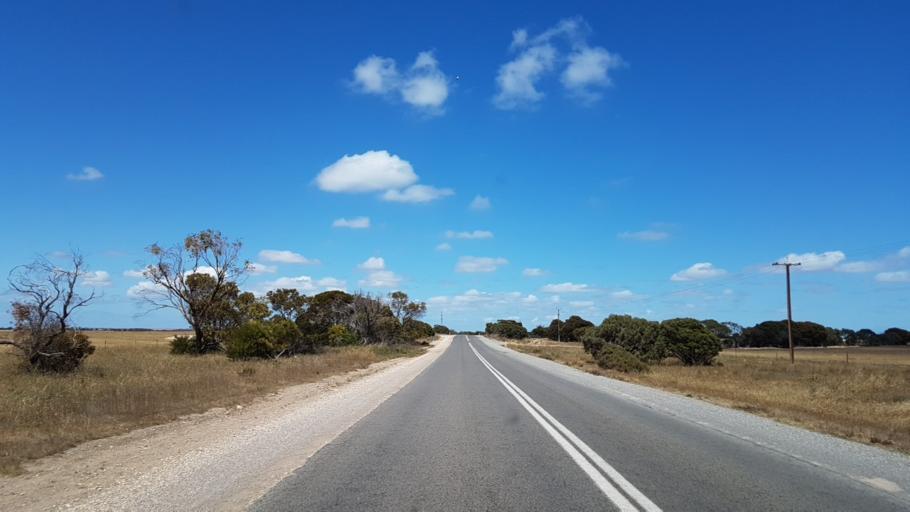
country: AU
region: South Australia
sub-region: Yorke Peninsula
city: Honiton
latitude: -34.8751
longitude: 137.4829
